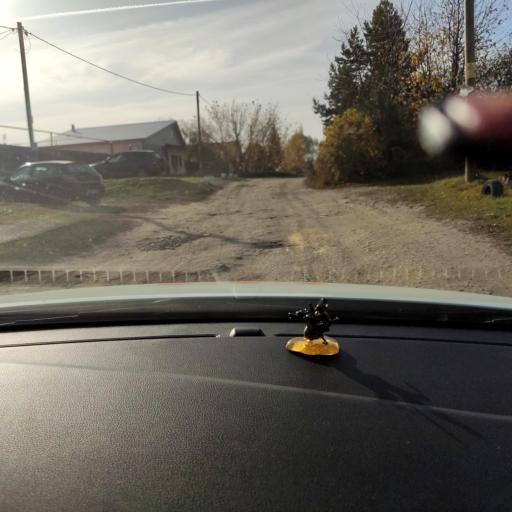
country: RU
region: Tatarstan
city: Vysokaya Gora
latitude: 55.7963
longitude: 49.2686
